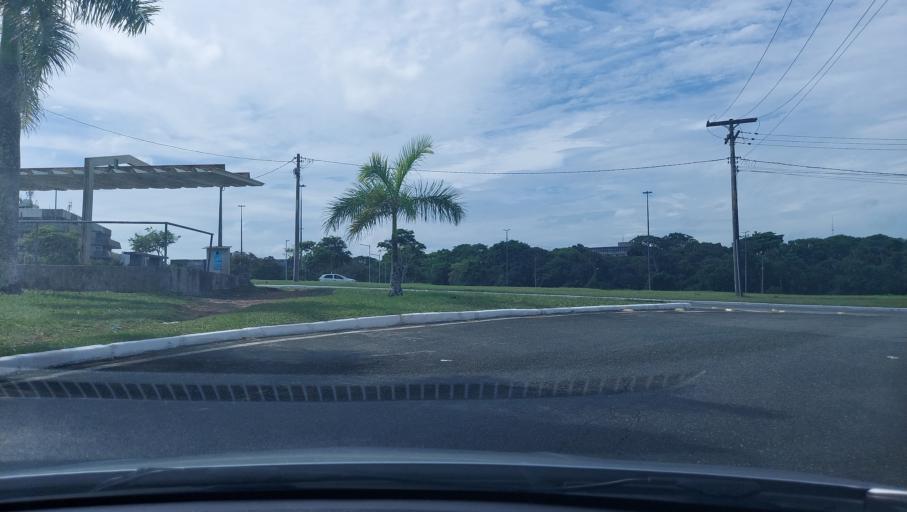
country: BR
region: Bahia
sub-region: Salvador
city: Salvador
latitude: -12.9487
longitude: -38.4287
